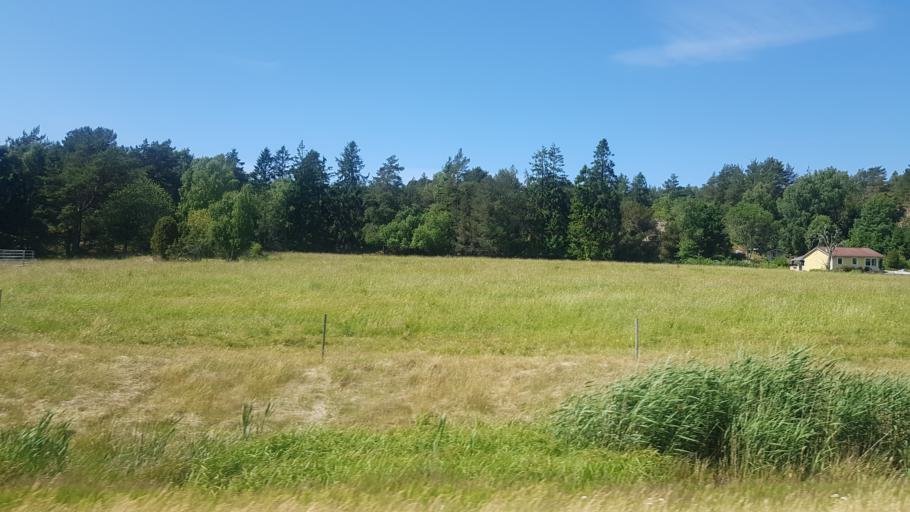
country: SE
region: Vaestra Goetaland
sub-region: Tjorns Kommun
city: Skaerhamn
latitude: 58.0102
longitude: 11.6105
